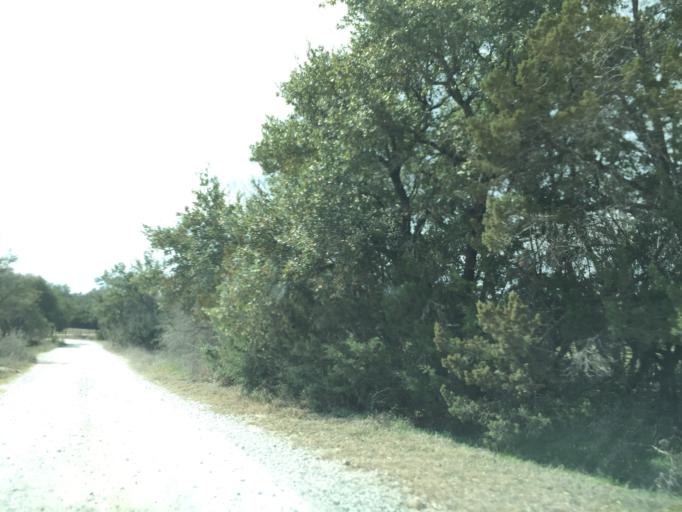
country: US
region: Texas
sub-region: Travis County
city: Briarcliff
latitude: 30.3872
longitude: -98.0941
